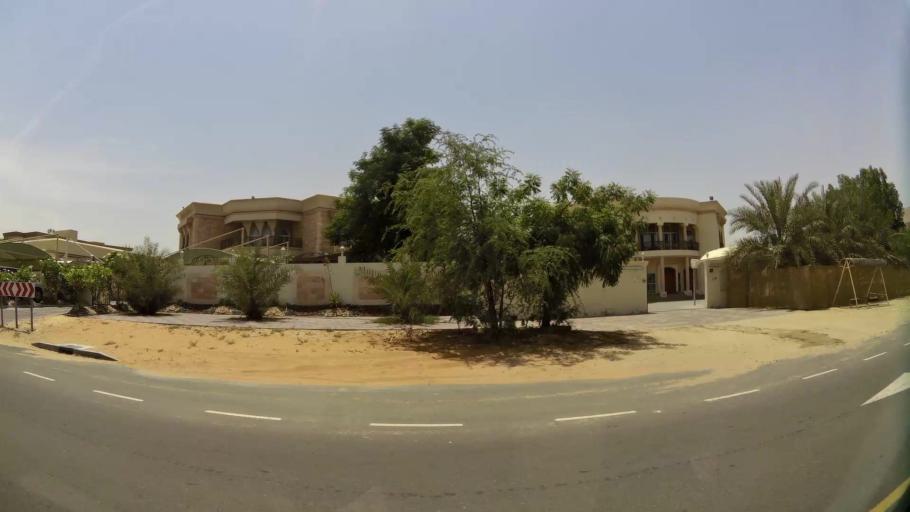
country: AE
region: Ash Shariqah
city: Sharjah
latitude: 25.2377
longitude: 55.4877
